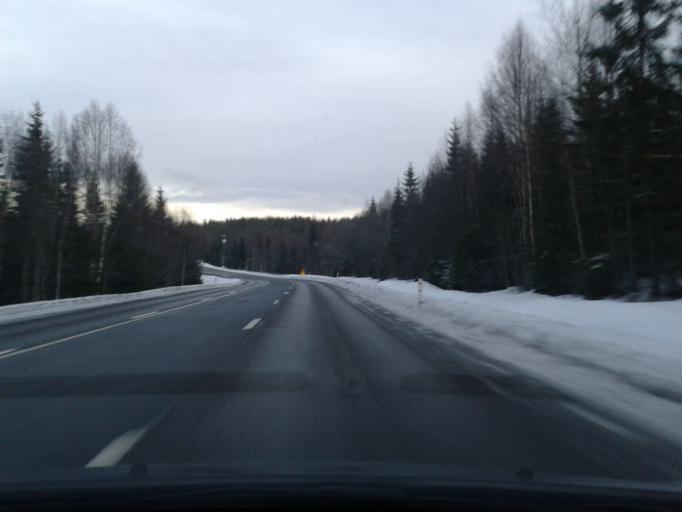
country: SE
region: Vaesternorrland
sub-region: Solleftea Kommun
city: Solleftea
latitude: 63.1306
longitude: 17.4700
